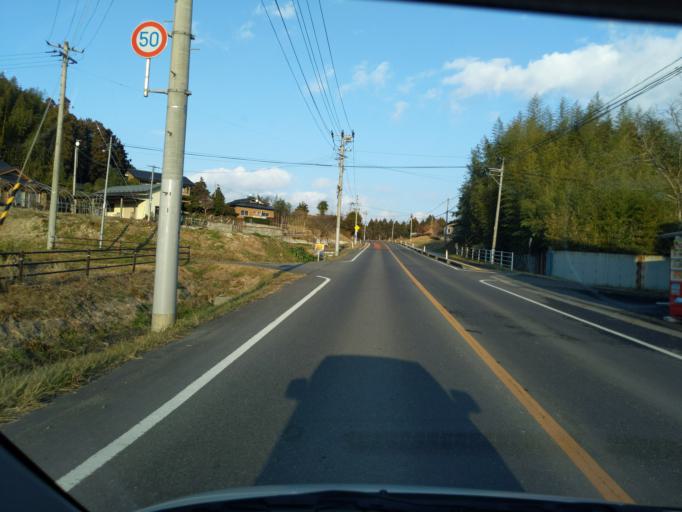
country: JP
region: Miyagi
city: Wakuya
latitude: 38.6811
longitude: 141.1297
